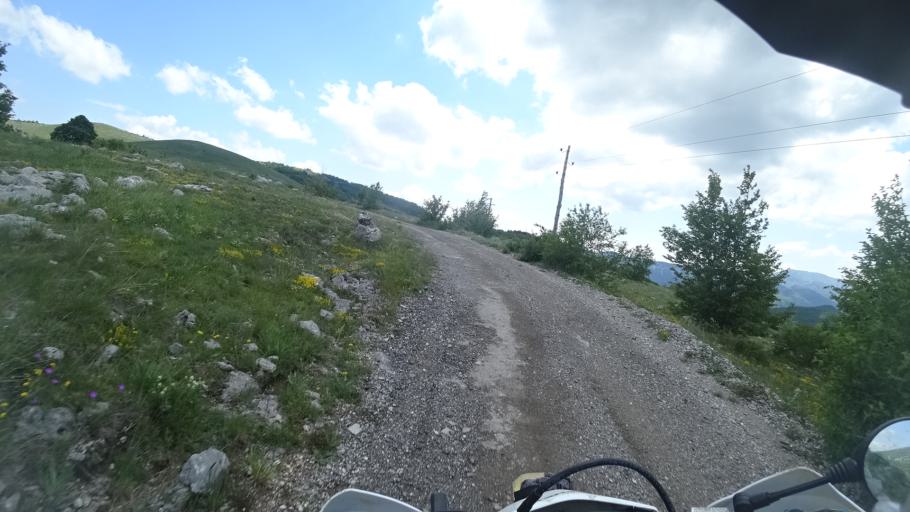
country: HR
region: Zadarska
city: Gracac
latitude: 44.3008
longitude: 15.9449
